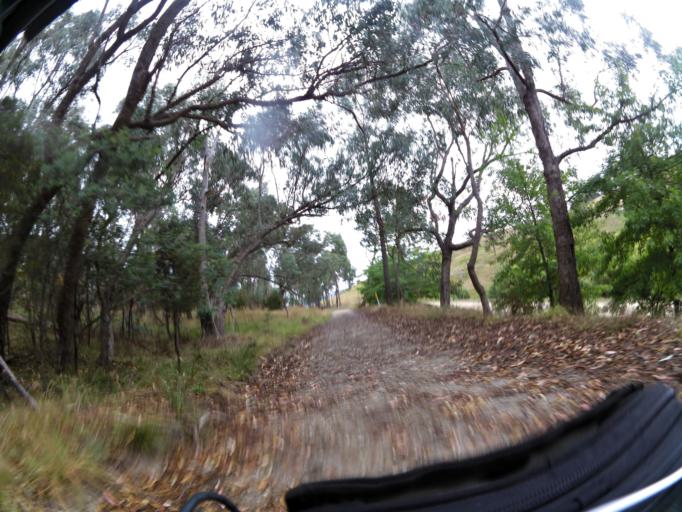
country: AU
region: New South Wales
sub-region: Greater Hume Shire
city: Holbrook
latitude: -36.1562
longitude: 147.4113
